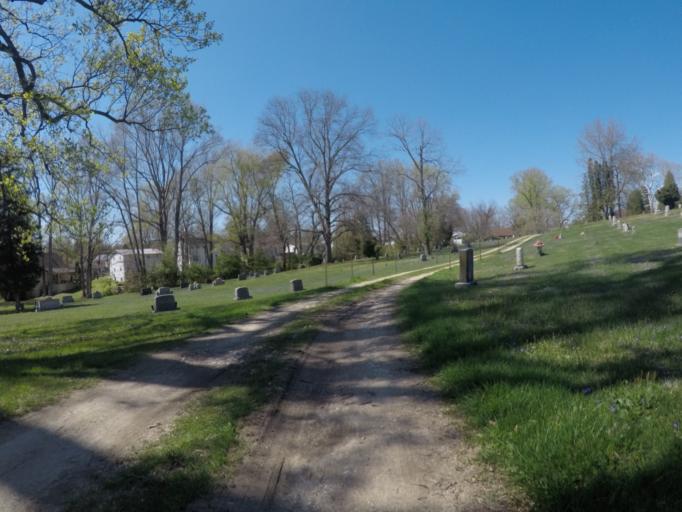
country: US
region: West Virginia
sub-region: Cabell County
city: Pea Ridge
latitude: 38.4161
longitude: -82.3079
